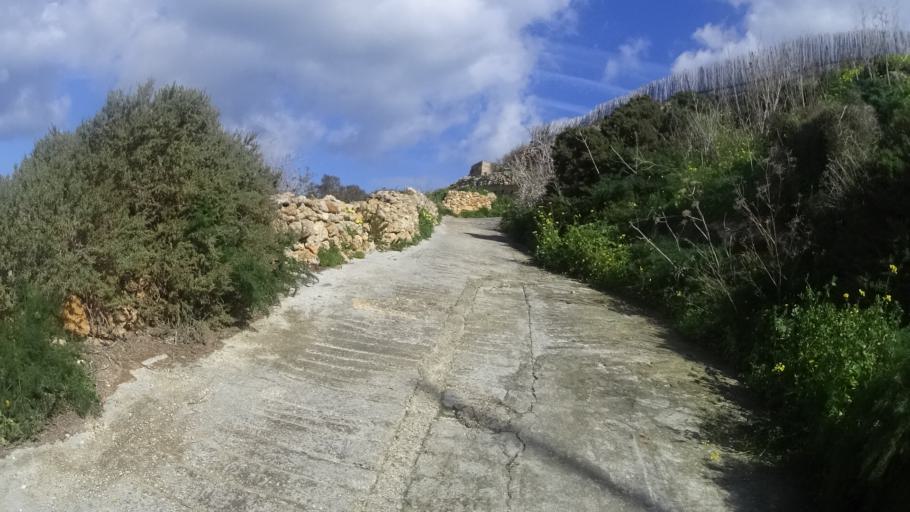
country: MT
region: In-Nadur
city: Nadur
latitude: 36.0500
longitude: 14.2991
